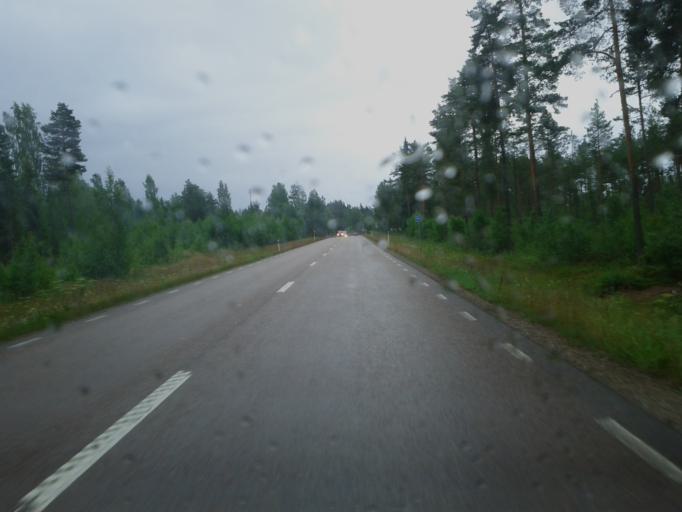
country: SE
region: Dalarna
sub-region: Mora Kommun
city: Mora
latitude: 60.9667
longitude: 14.7048
